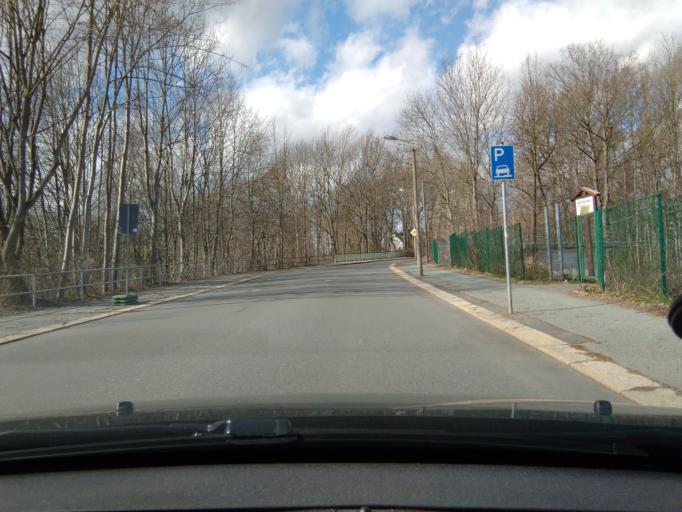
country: DE
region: Saxony
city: Wittgensdorf
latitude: 50.8338
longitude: 12.8788
